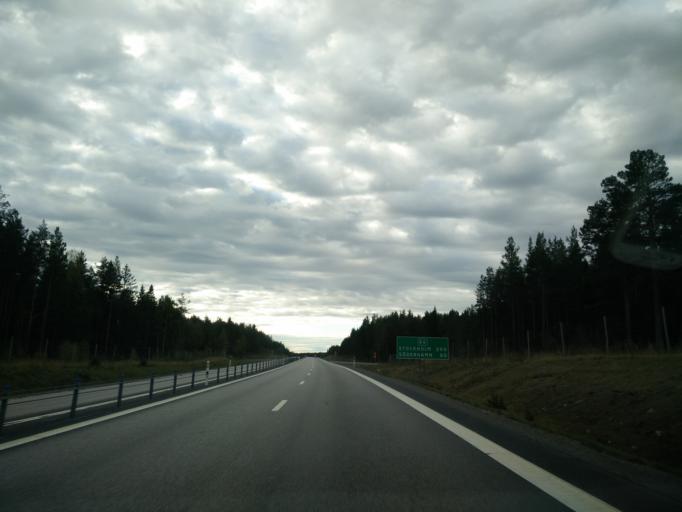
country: SE
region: Gaevleborg
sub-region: Hudiksvalls Kommun
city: Hudiksvall
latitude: 61.7084
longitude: 17.0494
